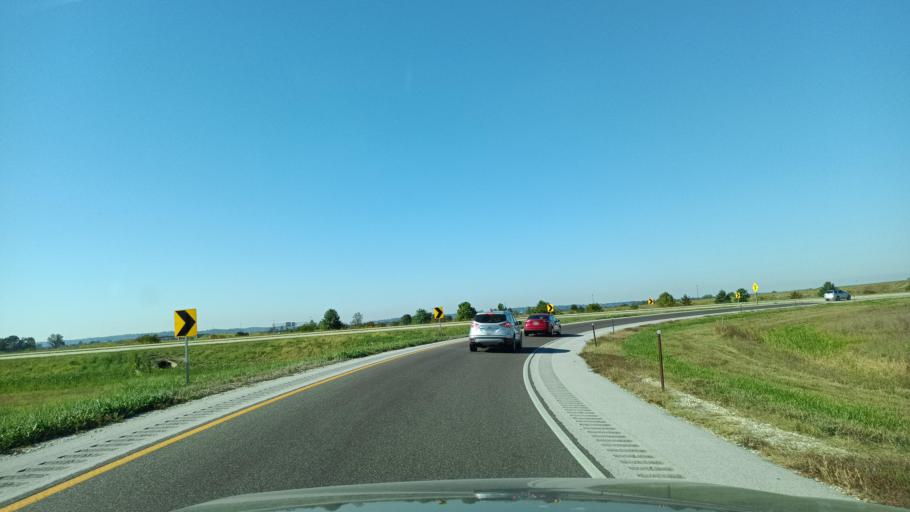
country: US
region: Illinois
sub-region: Adams County
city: Payson
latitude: 39.7612
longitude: -91.2875
